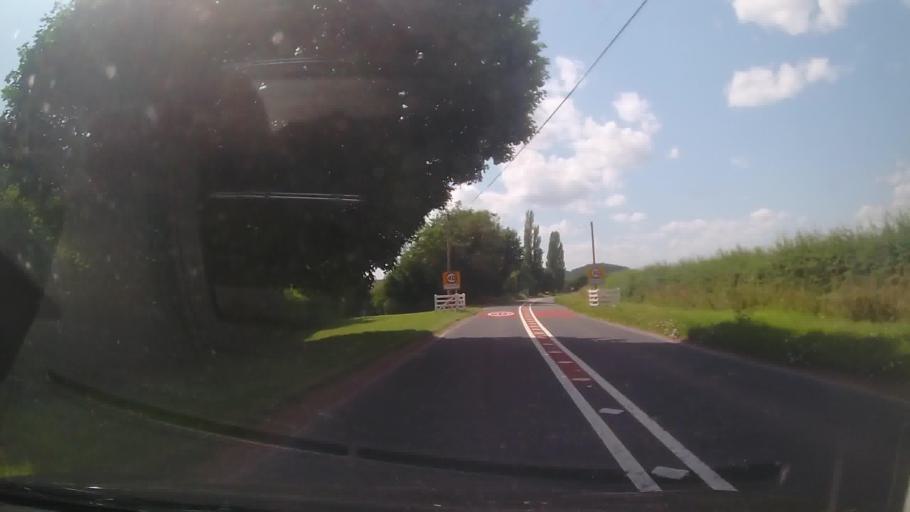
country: GB
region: England
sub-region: Herefordshire
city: Bodenham
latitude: 52.1581
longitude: -2.6658
